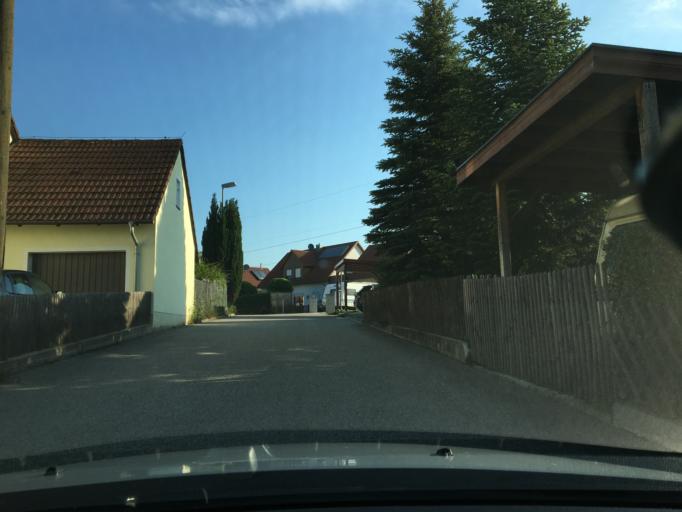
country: DE
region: Bavaria
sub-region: Lower Bavaria
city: Vilsbiburg
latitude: 48.4849
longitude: 12.3410
